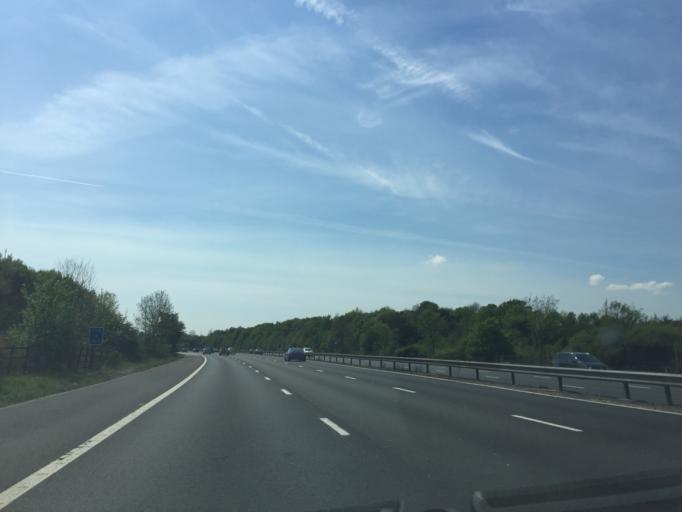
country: GB
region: England
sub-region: Essex
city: Chigwell
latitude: 51.6292
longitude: 0.0684
